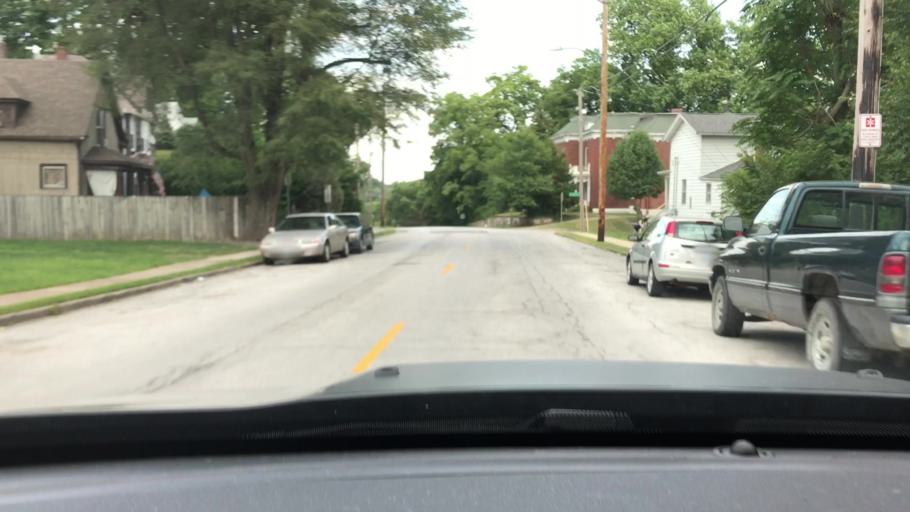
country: US
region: Iowa
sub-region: Scott County
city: Davenport
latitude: 41.5323
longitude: -90.5515
